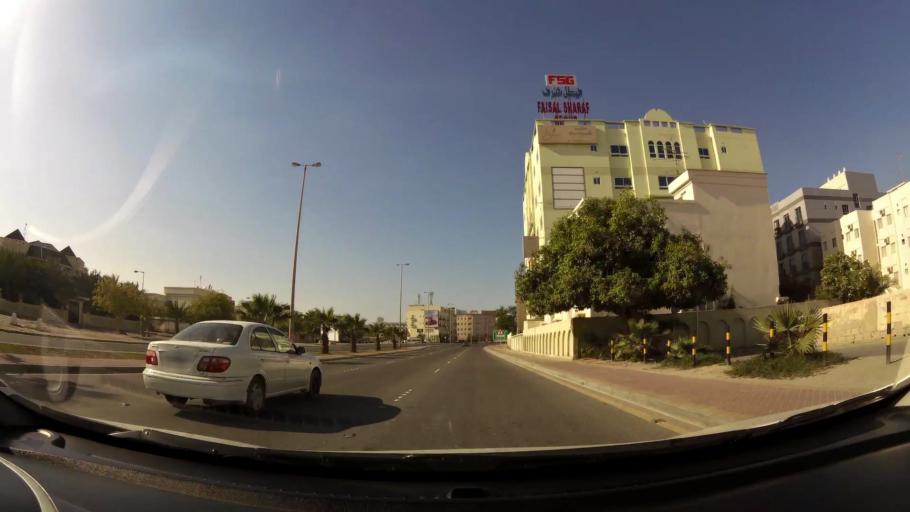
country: BH
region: Manama
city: Manama
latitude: 26.2099
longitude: 50.5666
